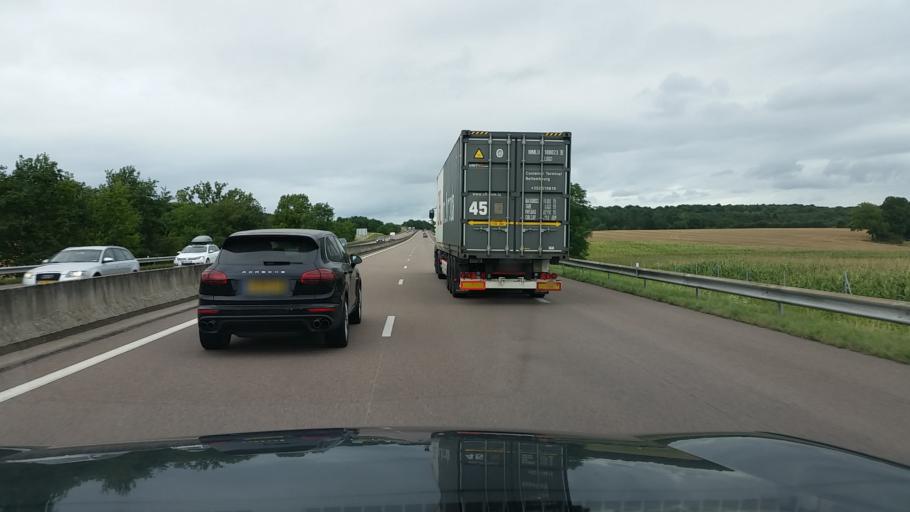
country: FR
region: Lorraine
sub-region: Departement des Vosges
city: Chatenois
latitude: 48.4141
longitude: 5.8650
